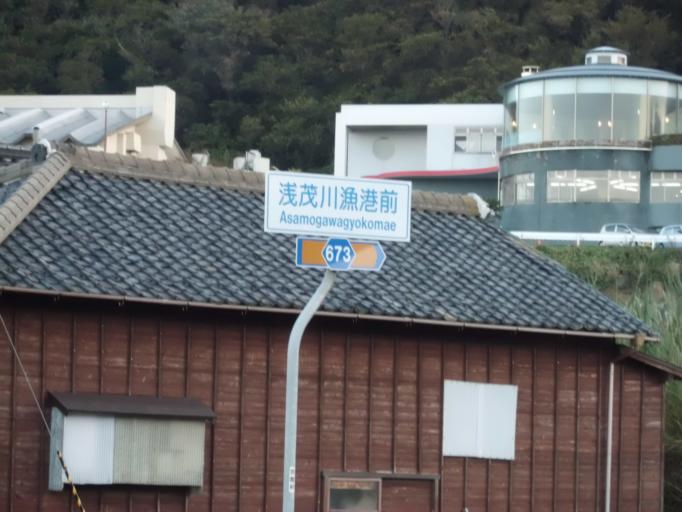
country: JP
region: Kyoto
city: Miyazu
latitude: 35.6910
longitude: 135.0128
